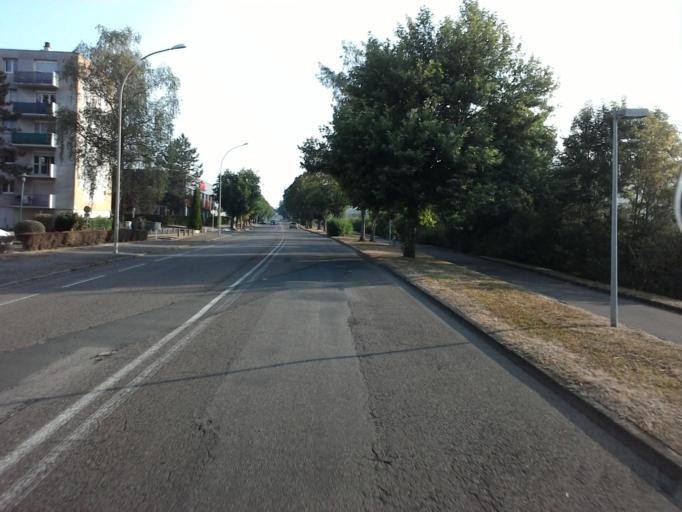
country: FR
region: Franche-Comte
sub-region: Departement de la Haute-Saone
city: Vesoul
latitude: 47.6231
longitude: 6.1707
